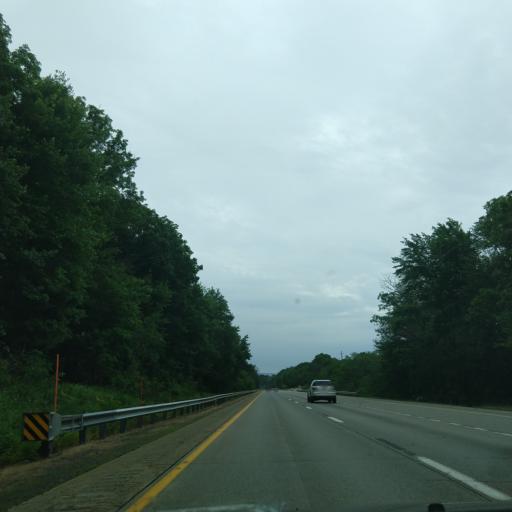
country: US
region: Pennsylvania
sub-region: Luzerne County
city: Nanticoke
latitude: 41.1558
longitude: -75.9587
